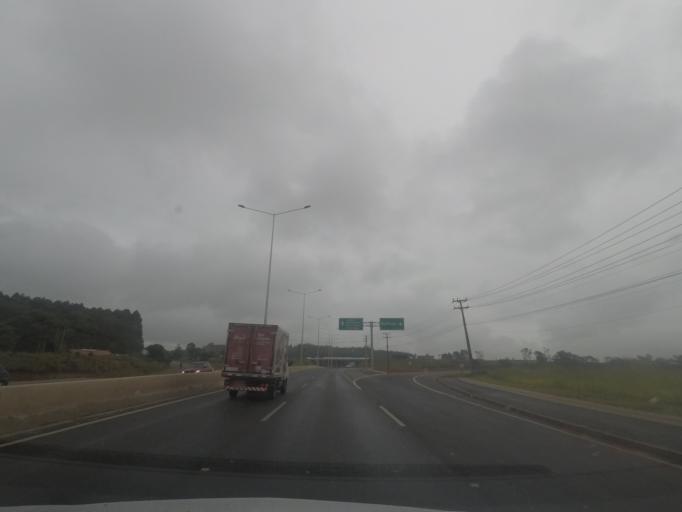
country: BR
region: Parana
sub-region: Piraquara
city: Piraquara
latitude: -25.4608
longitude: -49.0855
